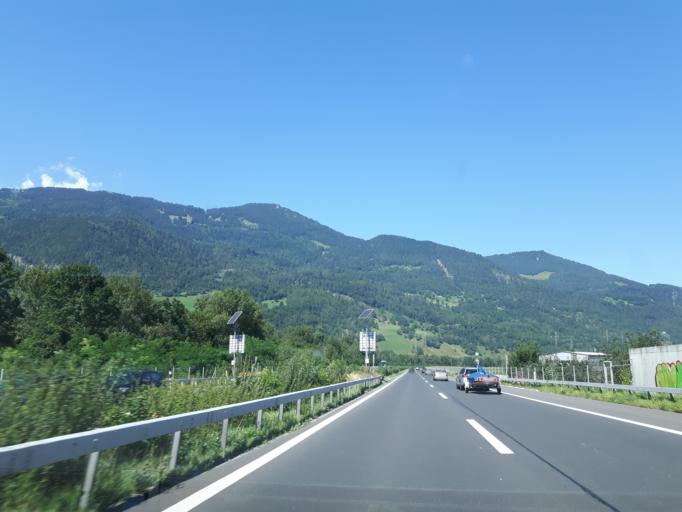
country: CH
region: Grisons
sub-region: Landquart District
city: Zizers
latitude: 46.9345
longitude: 9.5561
